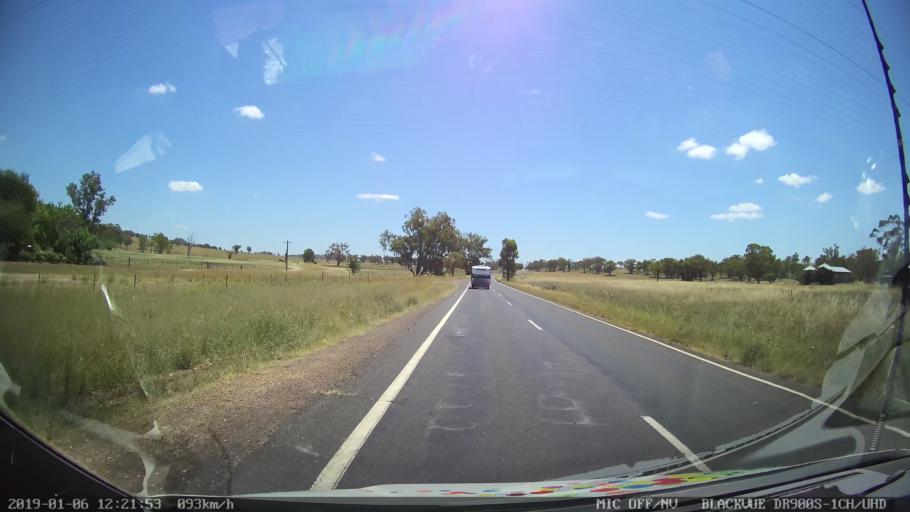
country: AU
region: New South Wales
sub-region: Tamworth Municipality
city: Phillip
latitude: -31.2684
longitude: 150.7845
